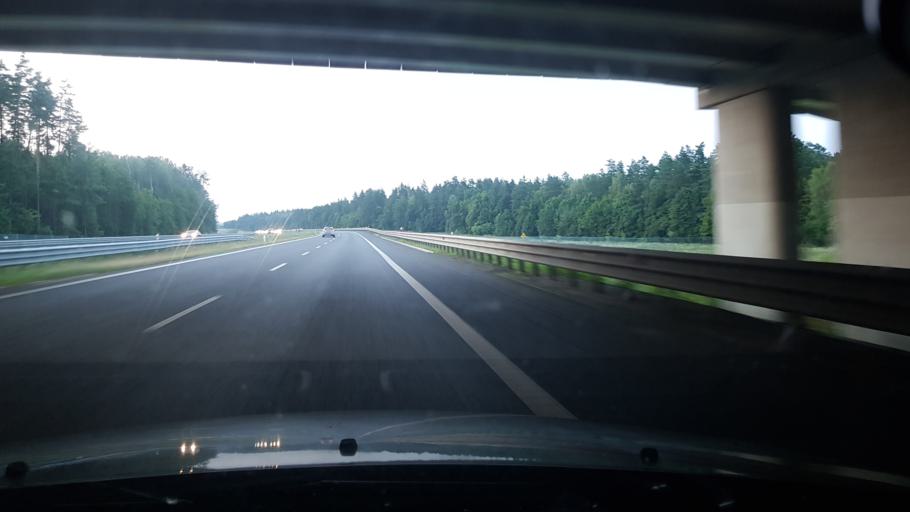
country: PL
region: Warmian-Masurian Voivodeship
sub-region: Powiat olsztynski
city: Olsztynek
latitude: 53.4608
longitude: 20.3223
